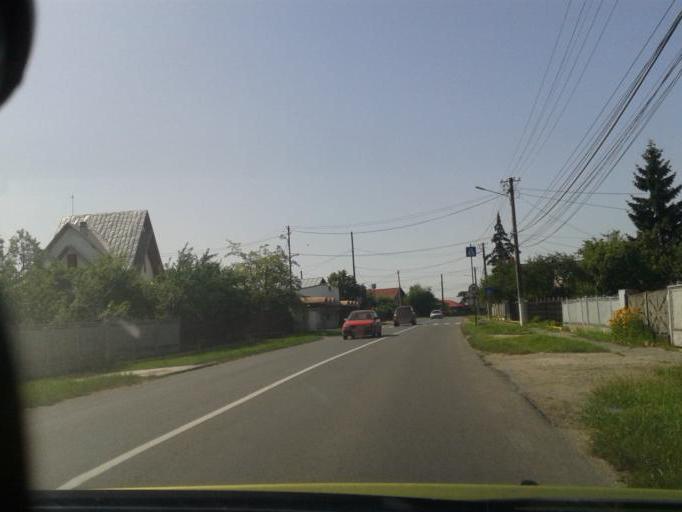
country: RO
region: Prahova
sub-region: Comuna Paulesti
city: Gageni
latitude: 45.0298
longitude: 25.9436
